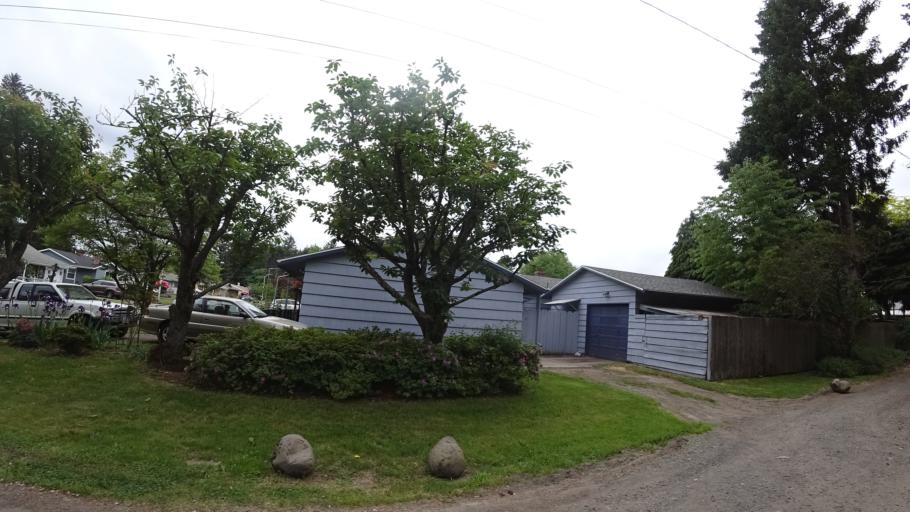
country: US
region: Oregon
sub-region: Multnomah County
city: Lents
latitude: 45.5094
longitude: -122.5222
